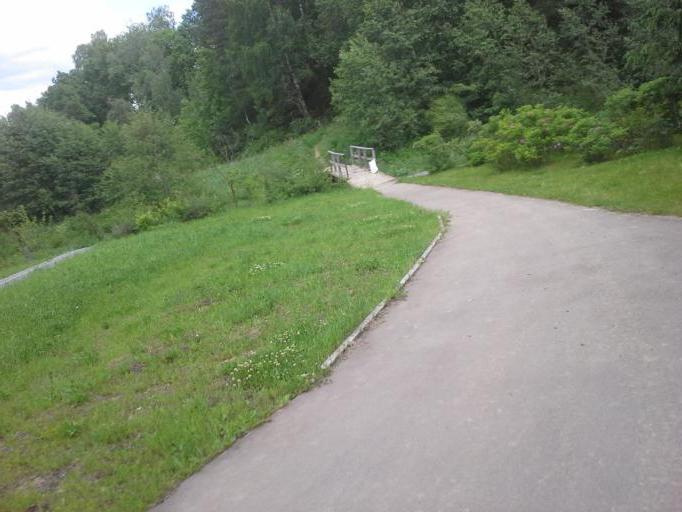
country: RU
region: Moskovskaya
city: Gorki Vtoryye
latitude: 55.6902
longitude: 37.1522
